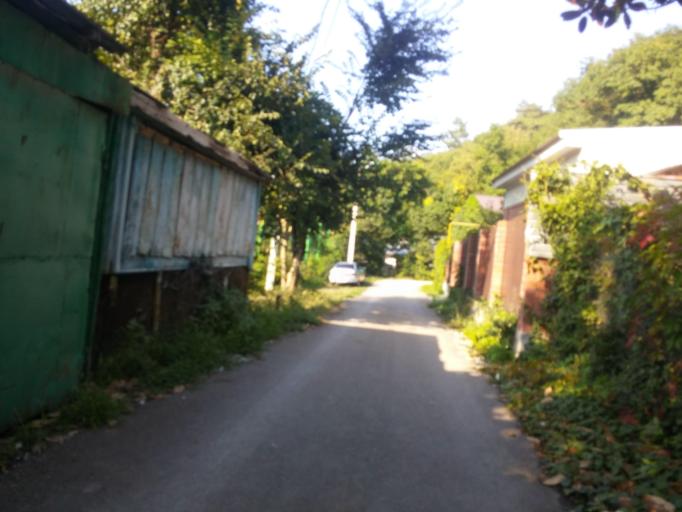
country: RU
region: Krasnodarskiy
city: Divnomorskoye
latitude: 44.4654
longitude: 38.1610
